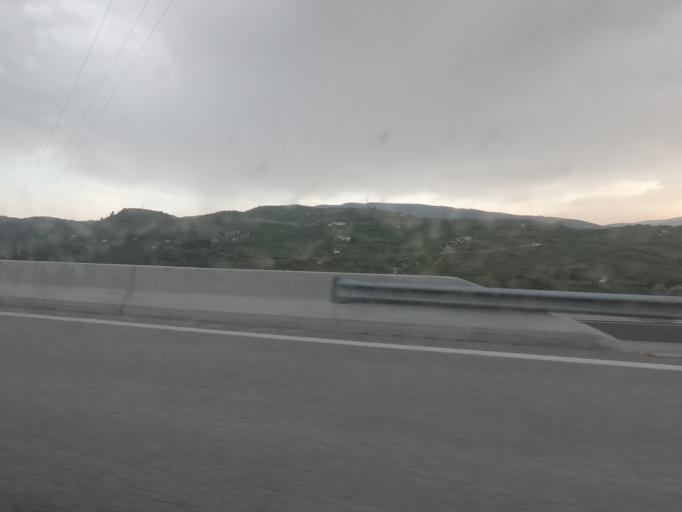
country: PT
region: Vila Real
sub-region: Peso da Regua
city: Peso da Regua
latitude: 41.1490
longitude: -7.7751
